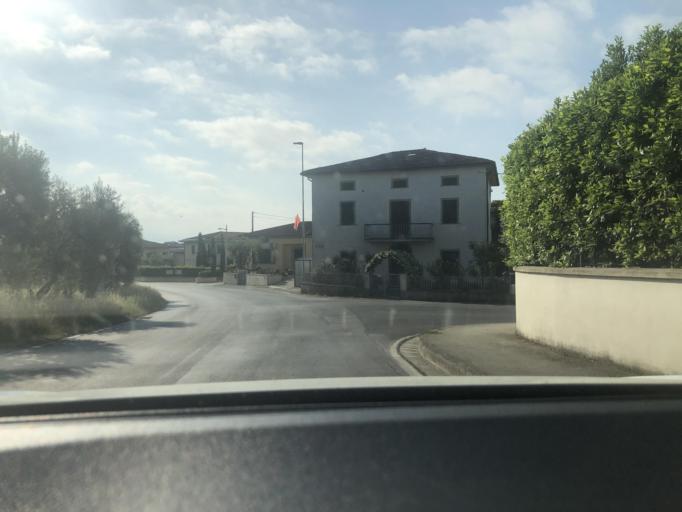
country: IT
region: Tuscany
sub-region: Provincia di Pistoia
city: Lamporecchio
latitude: 43.8062
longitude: 10.8700
